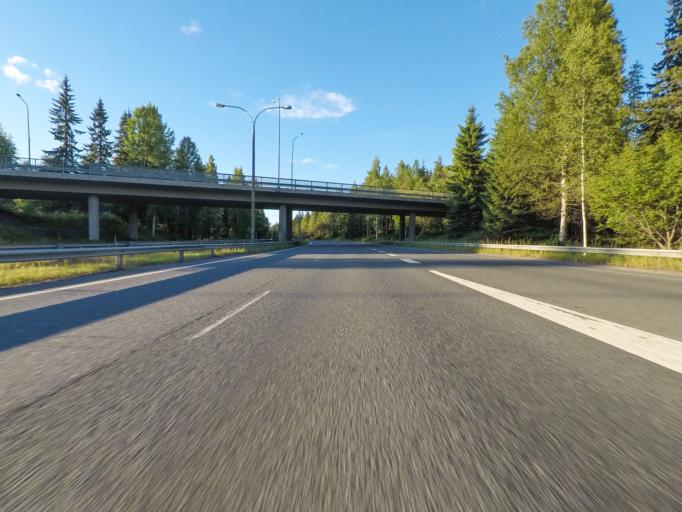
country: FI
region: Northern Savo
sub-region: Kuopio
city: Kuopio
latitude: 62.9037
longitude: 27.6827
